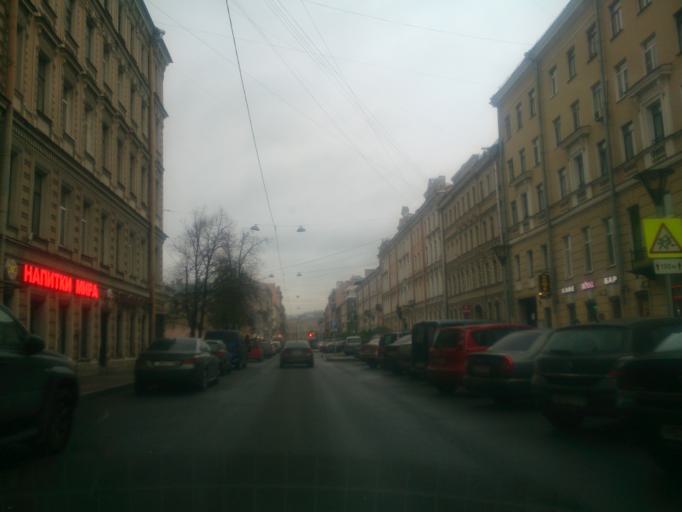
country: RU
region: St.-Petersburg
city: Centralniy
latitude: 59.9238
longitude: 30.3430
